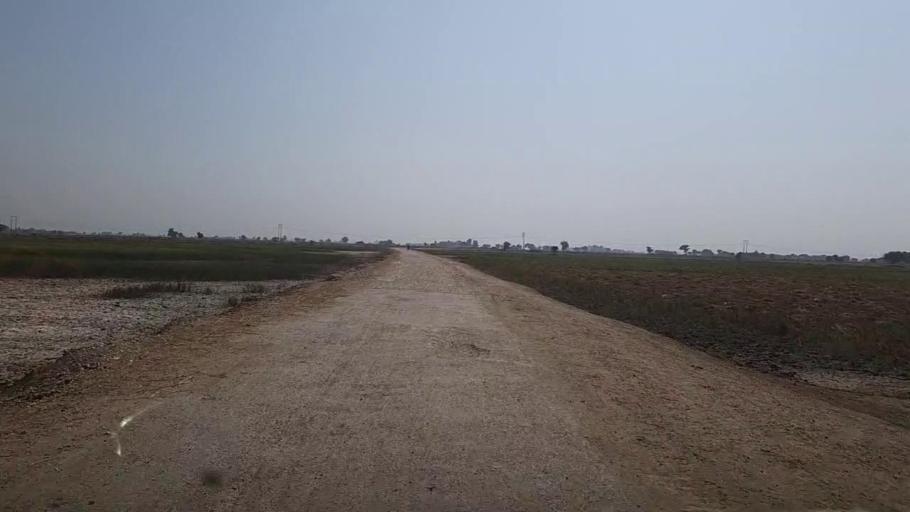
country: PK
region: Sindh
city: Kandhkot
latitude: 28.3930
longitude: 69.2933
